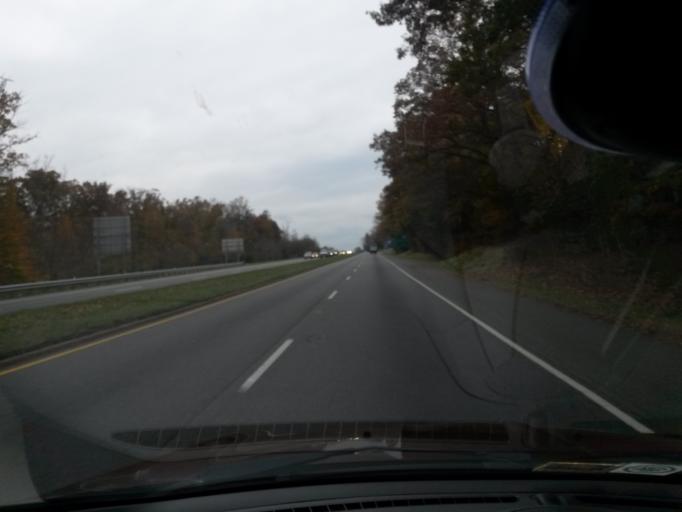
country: US
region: Virginia
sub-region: City of Charlottesville
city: Charlottesville
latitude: 38.0558
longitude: -78.5124
